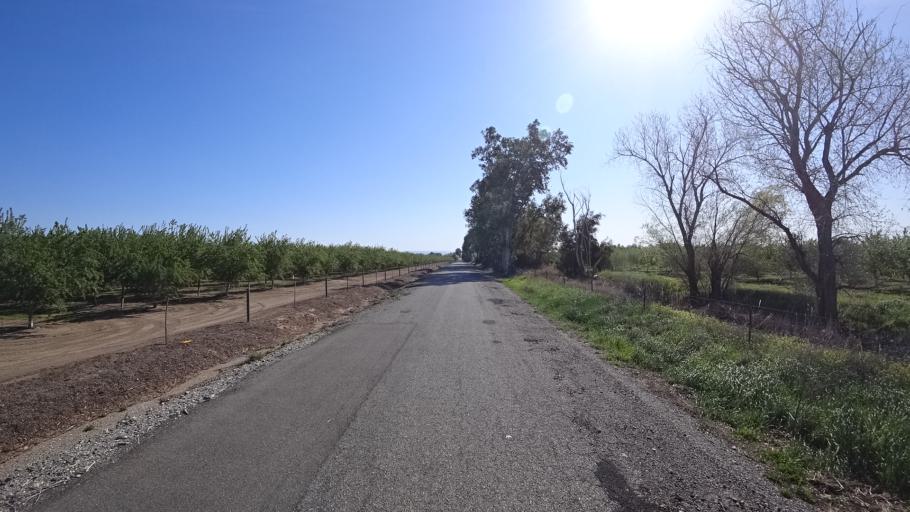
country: US
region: California
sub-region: Glenn County
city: Hamilton City
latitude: 39.7824
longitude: -122.0831
